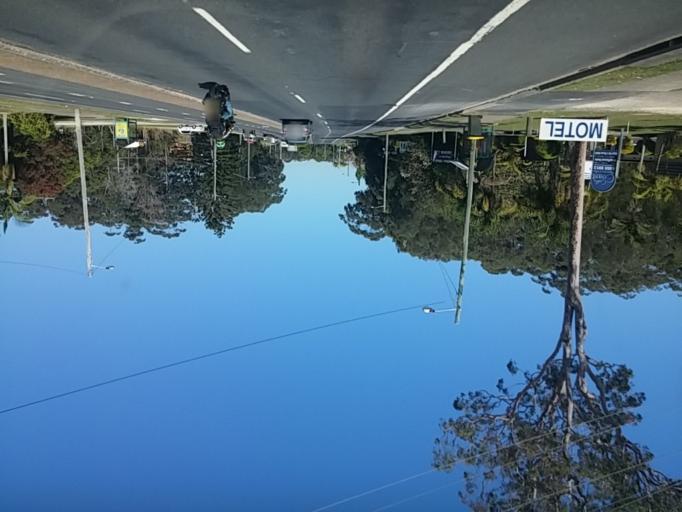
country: AU
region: New South Wales
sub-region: Coffs Harbour
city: Coffs Harbour
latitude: -30.2857
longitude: 153.1253
